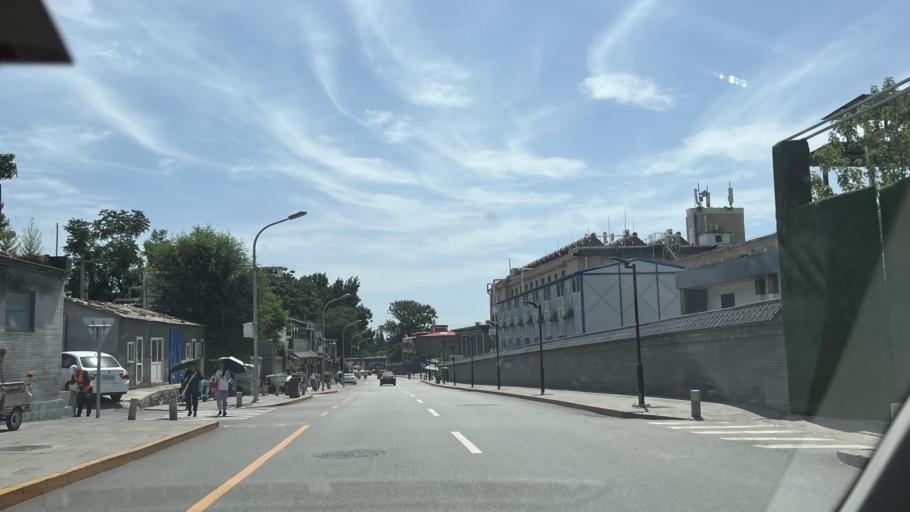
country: CN
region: Beijing
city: Xiangshan
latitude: 39.9918
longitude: 116.2012
